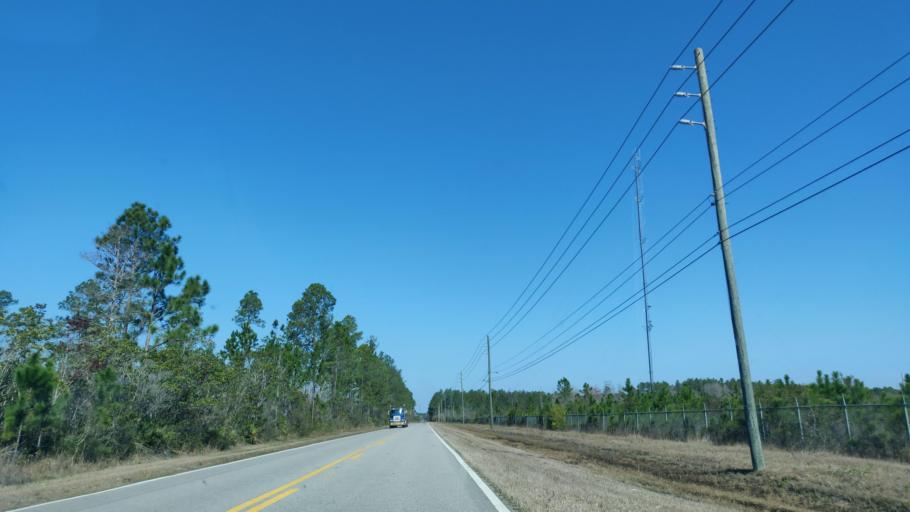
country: US
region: Florida
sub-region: Duval County
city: Baldwin
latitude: 30.2665
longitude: -81.9568
